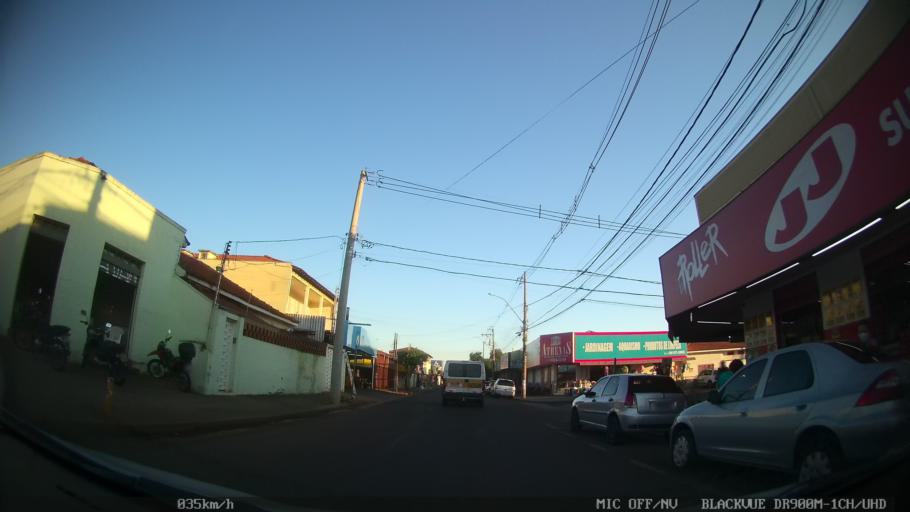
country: BR
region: Sao Paulo
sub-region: Sao Jose Do Rio Preto
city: Sao Jose do Rio Preto
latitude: -20.7909
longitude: -49.3695
